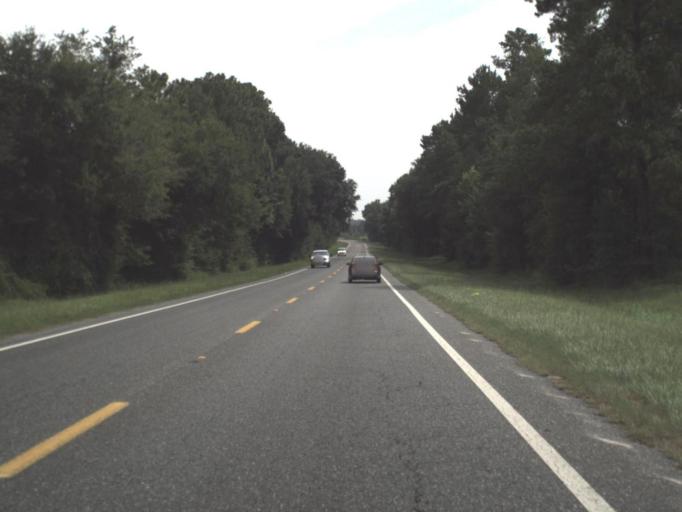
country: US
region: Florida
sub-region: Alachua County
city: High Springs
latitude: 29.9799
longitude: -82.5987
